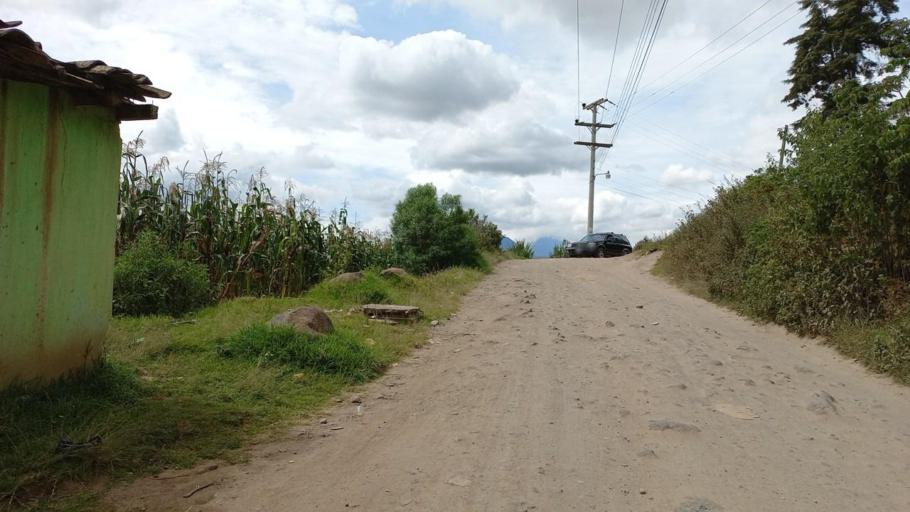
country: GT
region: Totonicapan
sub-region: Municipio de San Andres Xecul
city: San Andres Xecul
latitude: 14.8879
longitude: -91.4769
